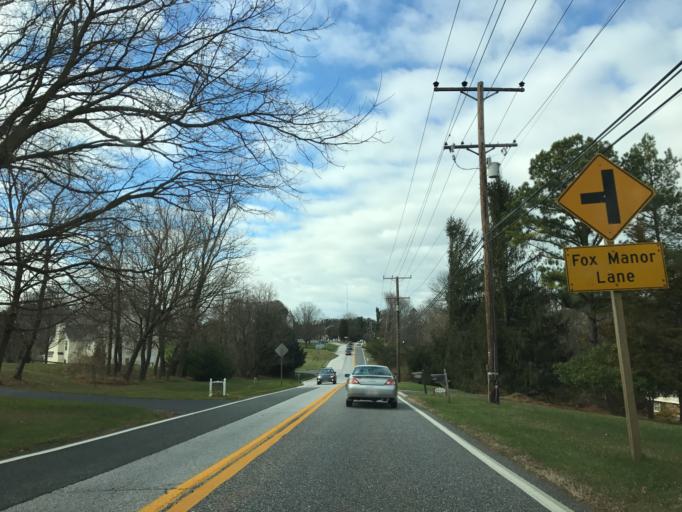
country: US
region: Maryland
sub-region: Baltimore County
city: Hampton
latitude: 39.5127
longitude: -76.5385
